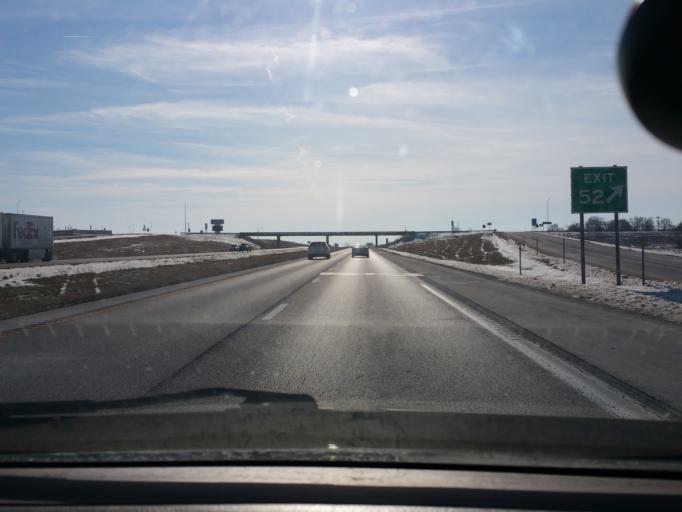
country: US
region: Missouri
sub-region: Clinton County
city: Cameron
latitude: 39.7342
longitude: -94.2206
